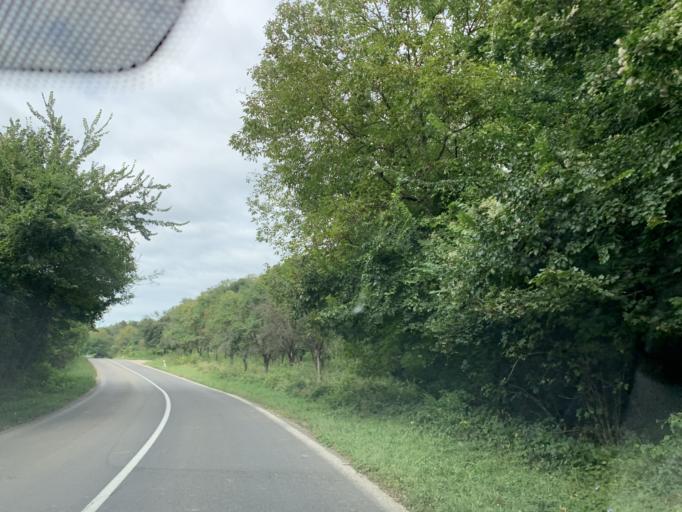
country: SK
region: Trenciansky
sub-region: Okres Nove Mesto nad Vahom
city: Nove Mesto nad Vahom
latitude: 48.8030
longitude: 17.9101
